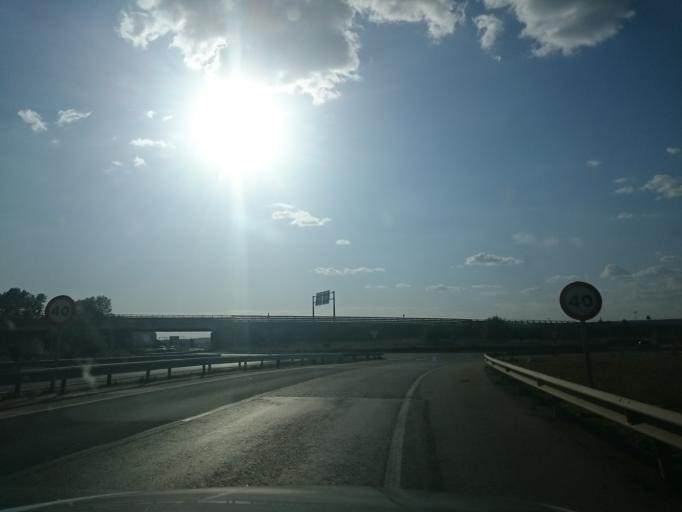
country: ES
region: Castille and Leon
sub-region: Provincia de Burgos
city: Cardenajimeno
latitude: 42.3442
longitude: -3.6363
